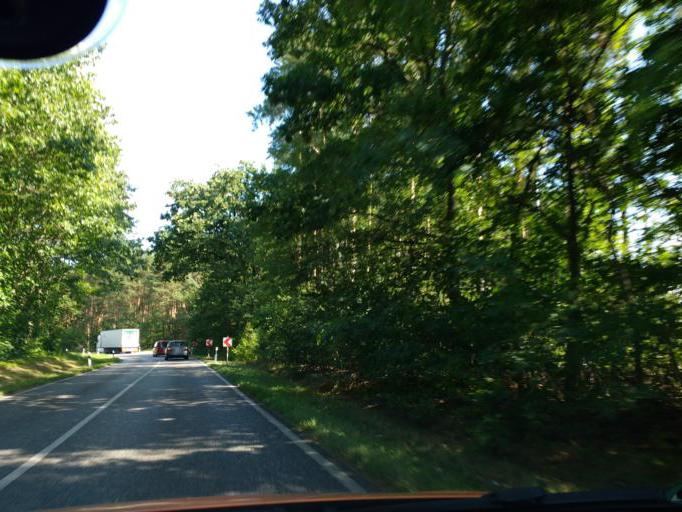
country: DE
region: Brandenburg
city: Birkenwerder
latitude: 52.7171
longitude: 13.2665
